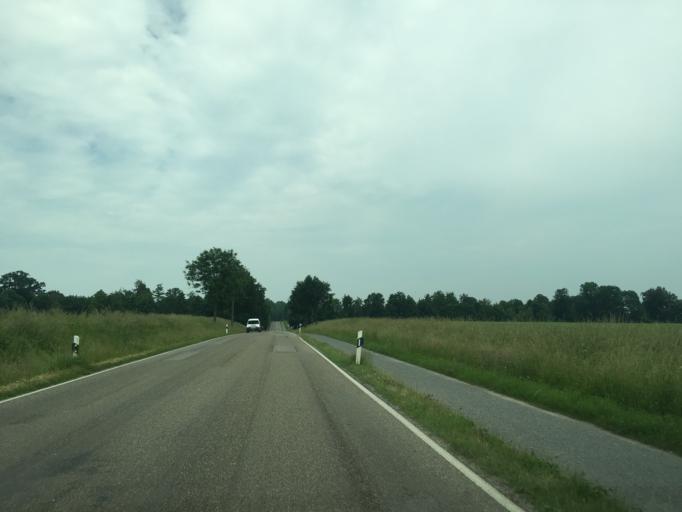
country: DE
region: North Rhine-Westphalia
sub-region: Regierungsbezirk Munster
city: Altenberge
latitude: 52.0613
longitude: 7.4853
